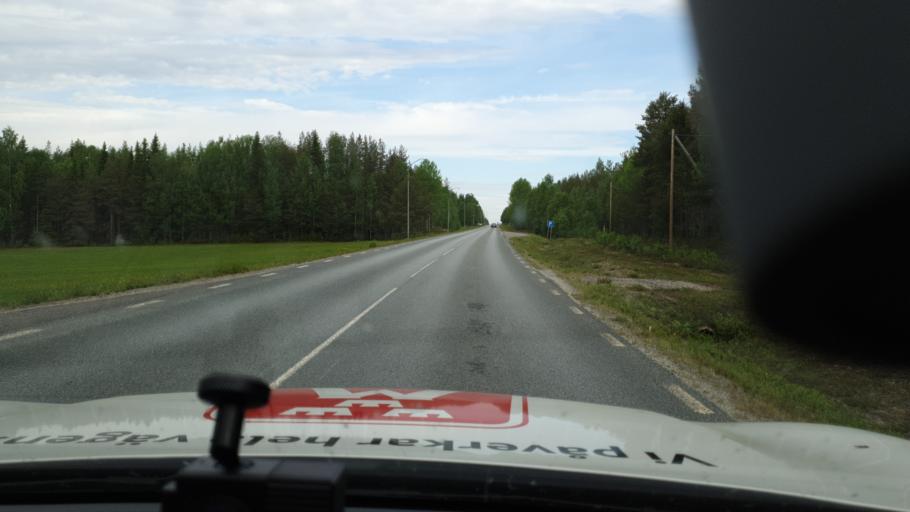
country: SE
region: Vaesterbotten
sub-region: Mala Kommun
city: Mala
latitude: 64.9914
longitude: 18.4927
